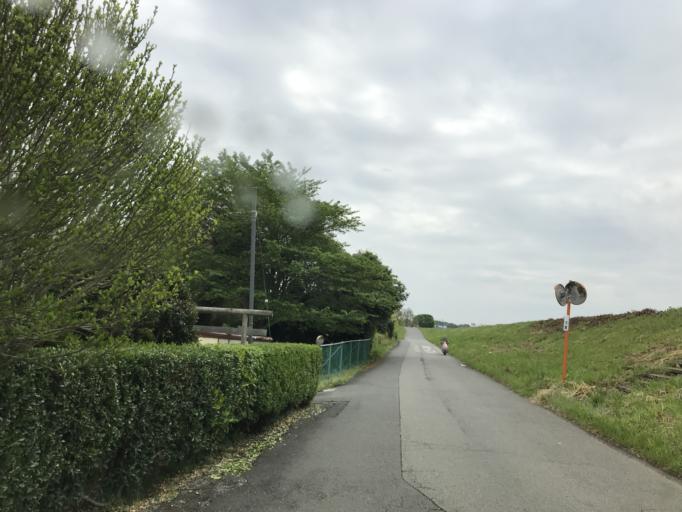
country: JP
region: Ibaraki
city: Mitsukaido
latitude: 35.9963
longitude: 139.9783
